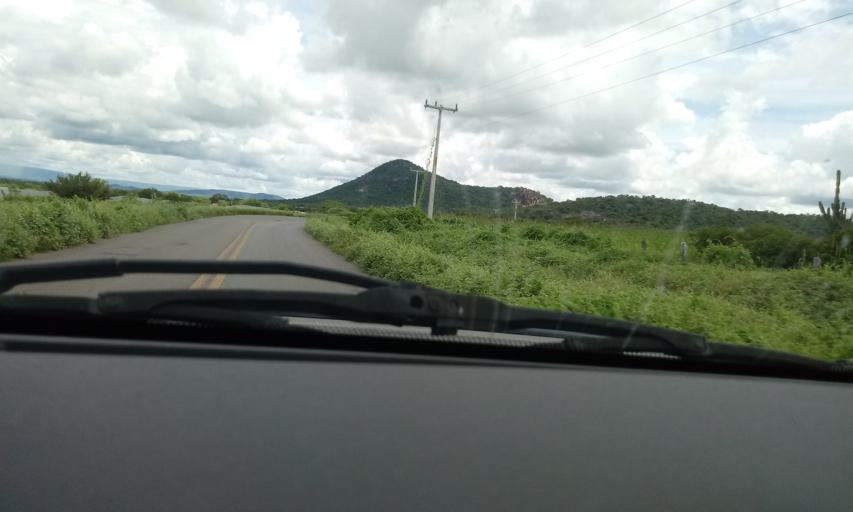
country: BR
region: Bahia
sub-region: Guanambi
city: Guanambi
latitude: -14.1469
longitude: -42.8345
